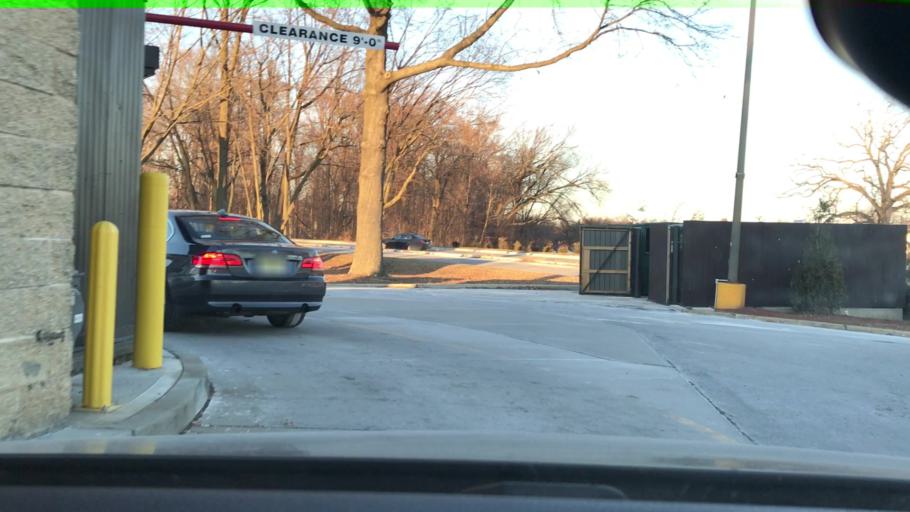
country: US
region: New Jersey
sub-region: Morris County
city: Morris Plains
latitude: 40.8438
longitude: -74.4627
